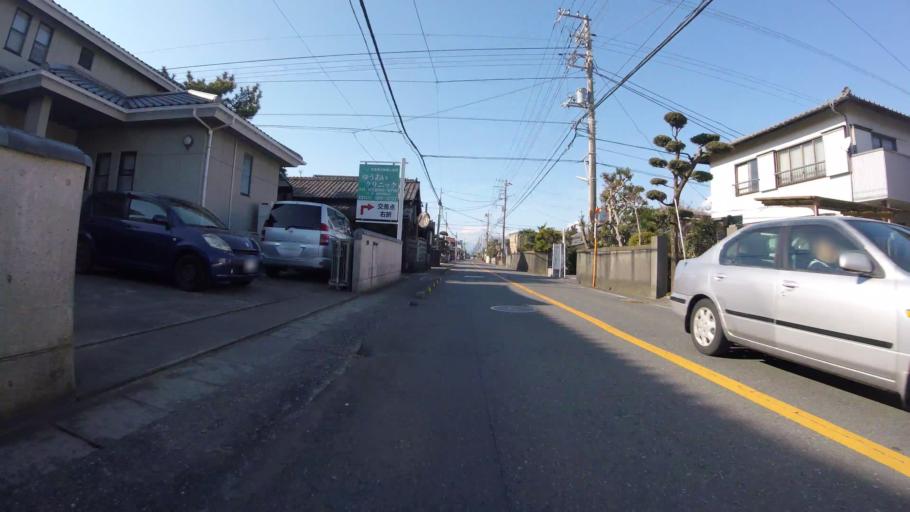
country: JP
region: Shizuoka
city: Numazu
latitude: 35.1147
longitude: 138.8231
